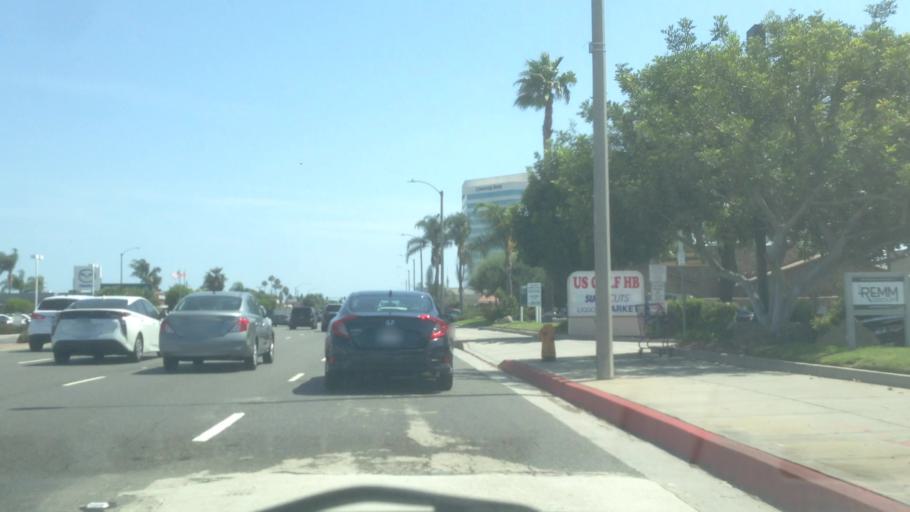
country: US
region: California
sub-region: Orange County
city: Midway City
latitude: 33.7189
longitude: -117.9894
